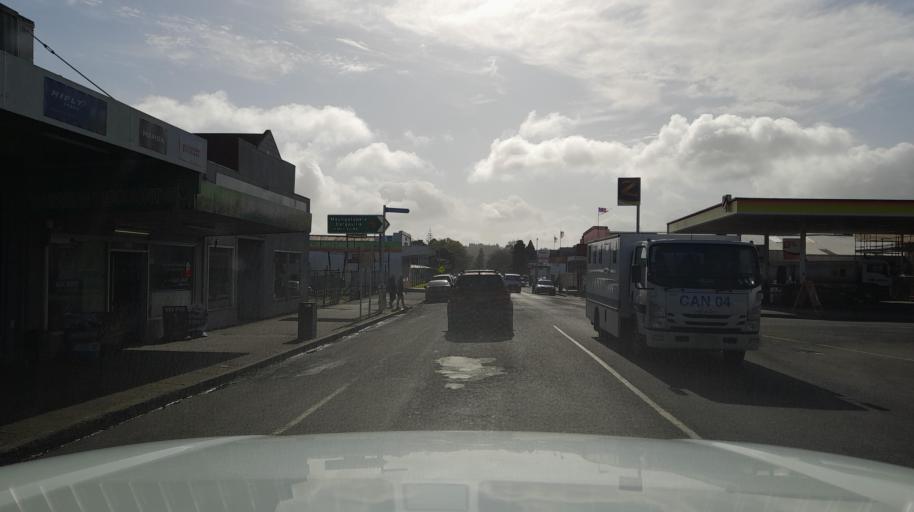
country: NZ
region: Northland
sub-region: Far North District
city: Waimate North
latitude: -35.4062
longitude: 173.8028
